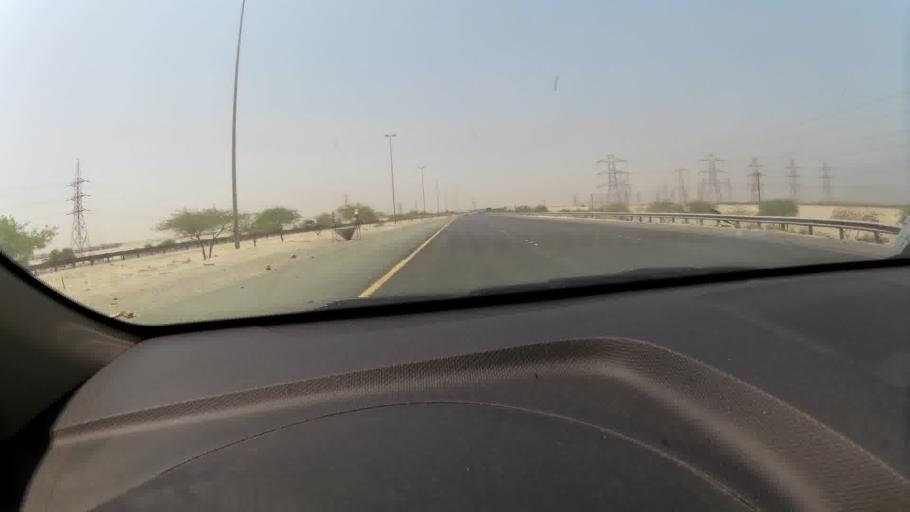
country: KW
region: Al Ahmadi
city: Al Fahahil
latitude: 28.9514
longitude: 48.1312
